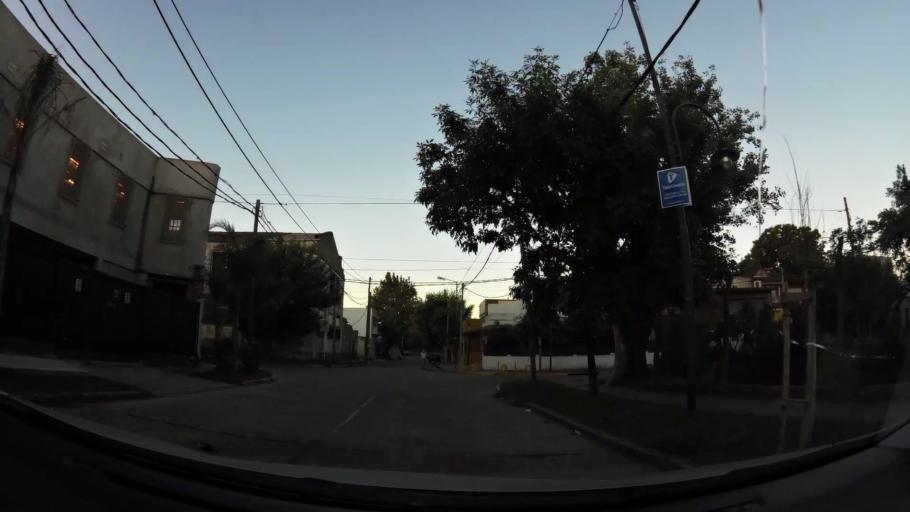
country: AR
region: Buenos Aires
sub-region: Partido de Tigre
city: Tigre
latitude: -34.4441
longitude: -58.5627
